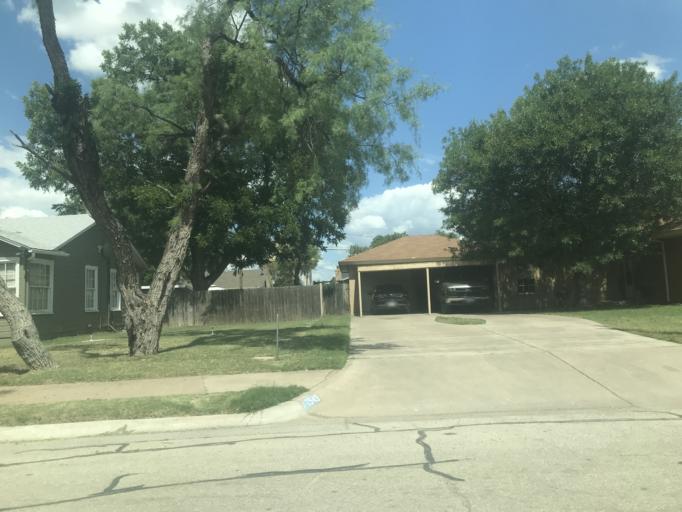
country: US
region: Texas
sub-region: Taylor County
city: Abilene
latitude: 32.4259
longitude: -99.7526
